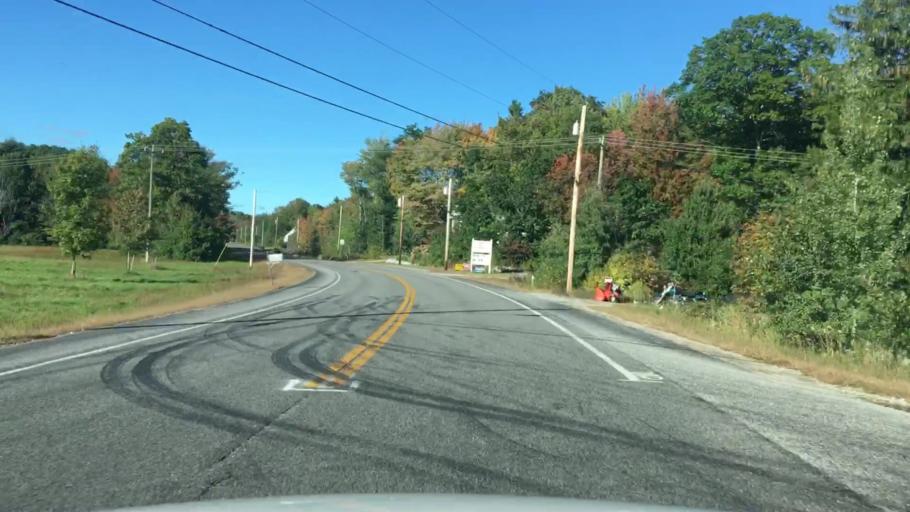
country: US
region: Maine
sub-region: Androscoggin County
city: Lisbon Falls
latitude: 44.0164
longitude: -70.0676
